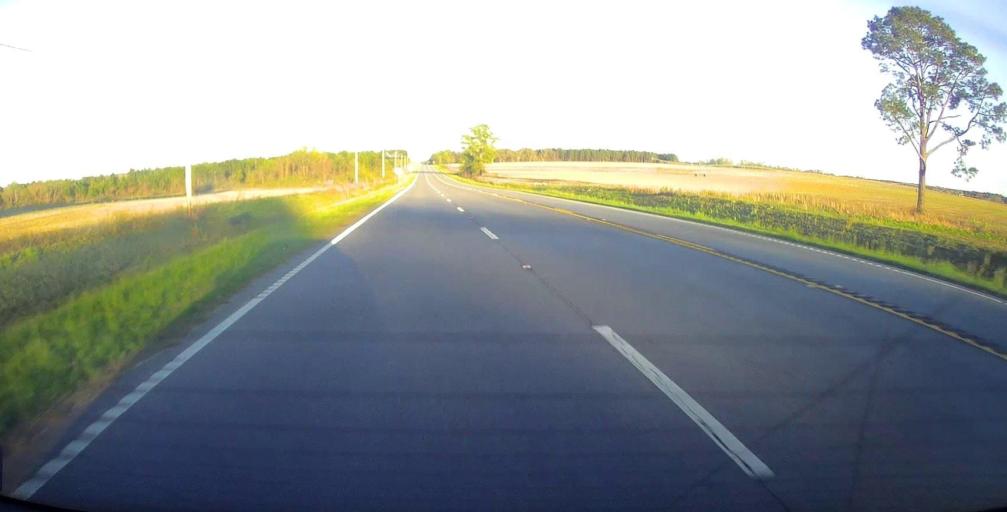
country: US
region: Georgia
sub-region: Crisp County
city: Cordele
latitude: 31.9571
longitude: -83.6502
